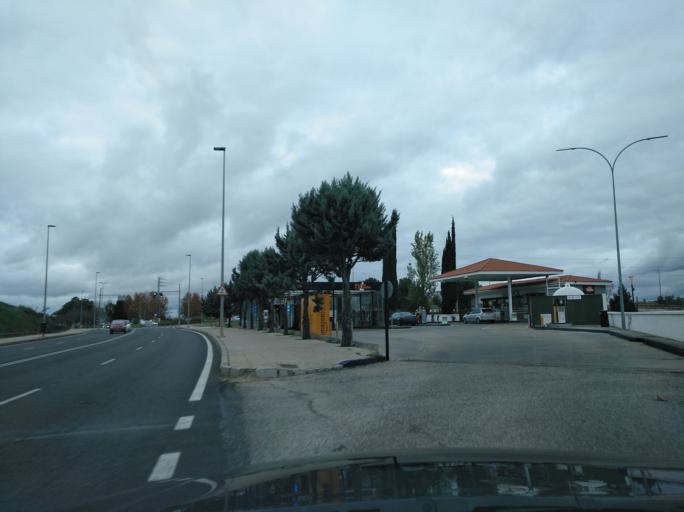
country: ES
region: Extremadura
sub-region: Provincia de Badajoz
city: Badajoz
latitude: 38.8813
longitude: -6.9641
